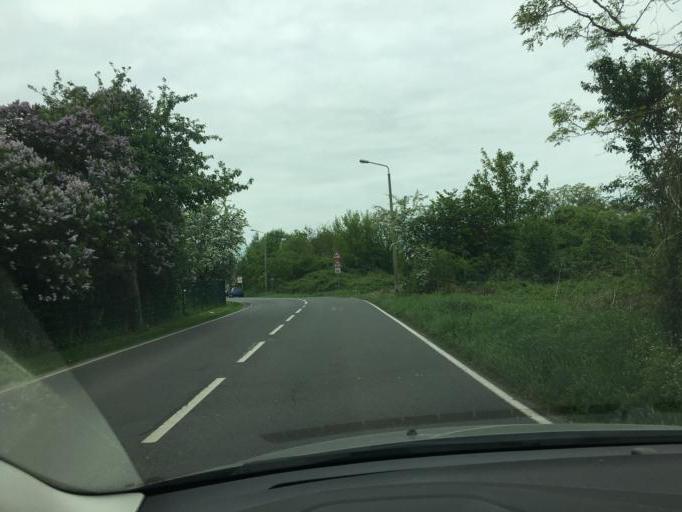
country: DE
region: Saxony
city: Taucha
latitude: 51.3666
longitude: 12.4449
